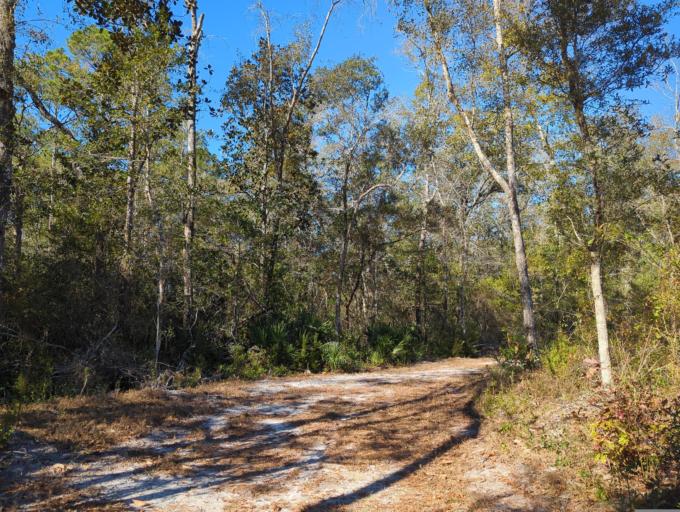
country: US
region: Florida
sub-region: Wakulla County
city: Crawfordville
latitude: 30.1851
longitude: -84.3302
